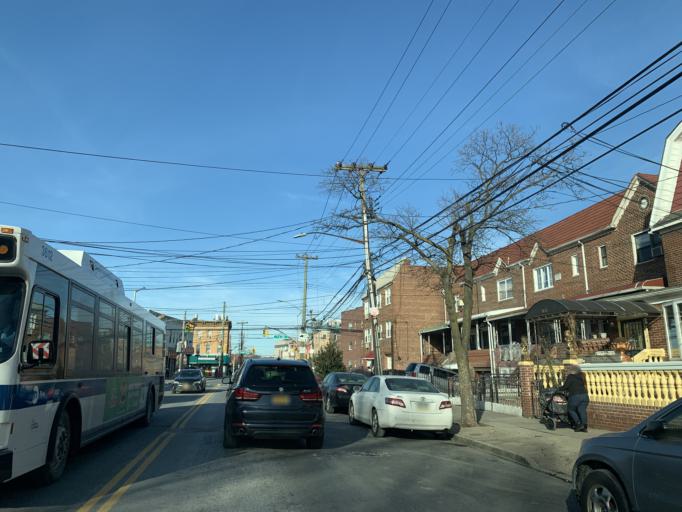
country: US
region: New York
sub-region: Queens County
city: Borough of Queens
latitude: 40.7411
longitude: -73.8675
